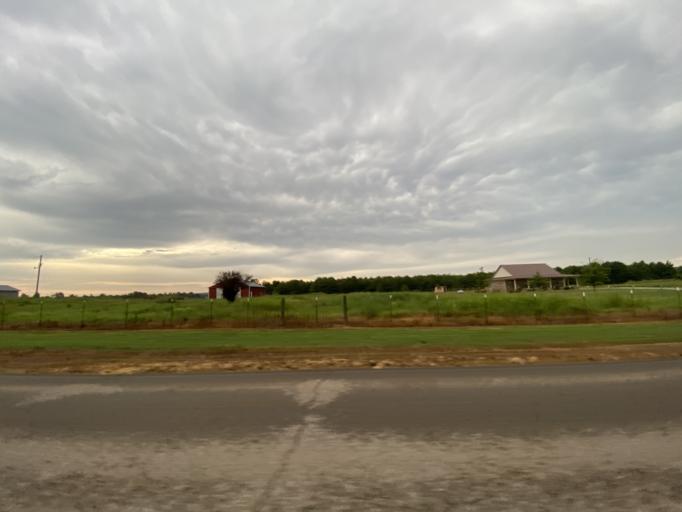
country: US
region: Alabama
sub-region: Lawrence County
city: Moulton
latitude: 34.4641
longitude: -87.5006
